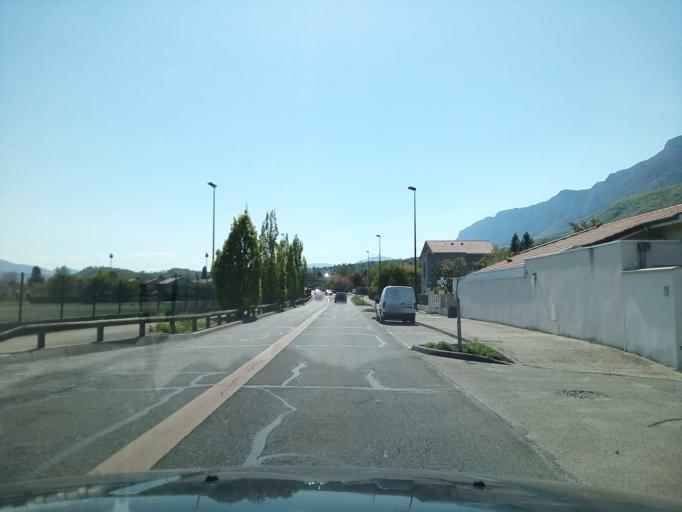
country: FR
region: Rhone-Alpes
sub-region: Departement de l'Isere
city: Crolles
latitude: 45.2807
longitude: 5.8775
